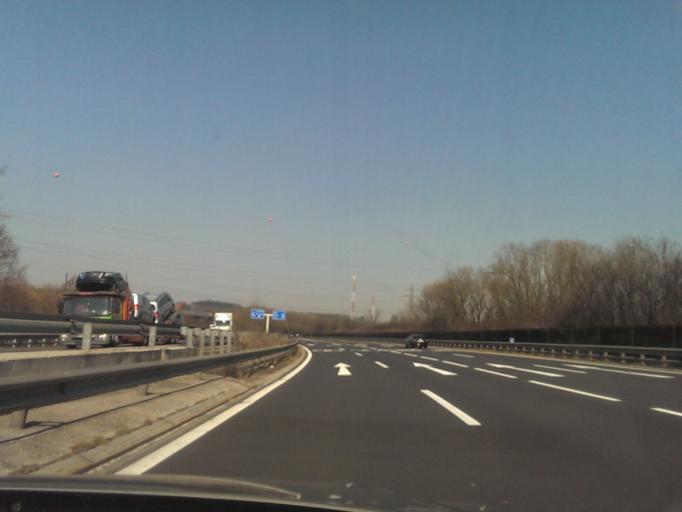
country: AT
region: Upper Austria
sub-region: Wels Stadt
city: Wels
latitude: 48.1726
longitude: 13.9927
